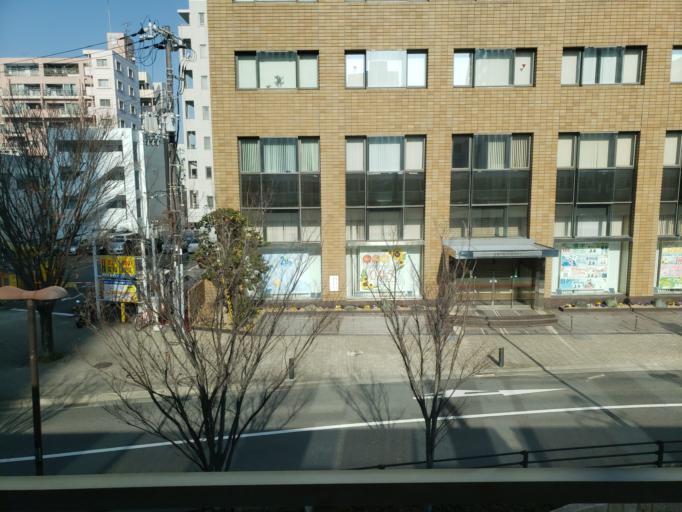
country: JP
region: Hyogo
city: Kobe
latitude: 34.6579
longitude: 135.1452
